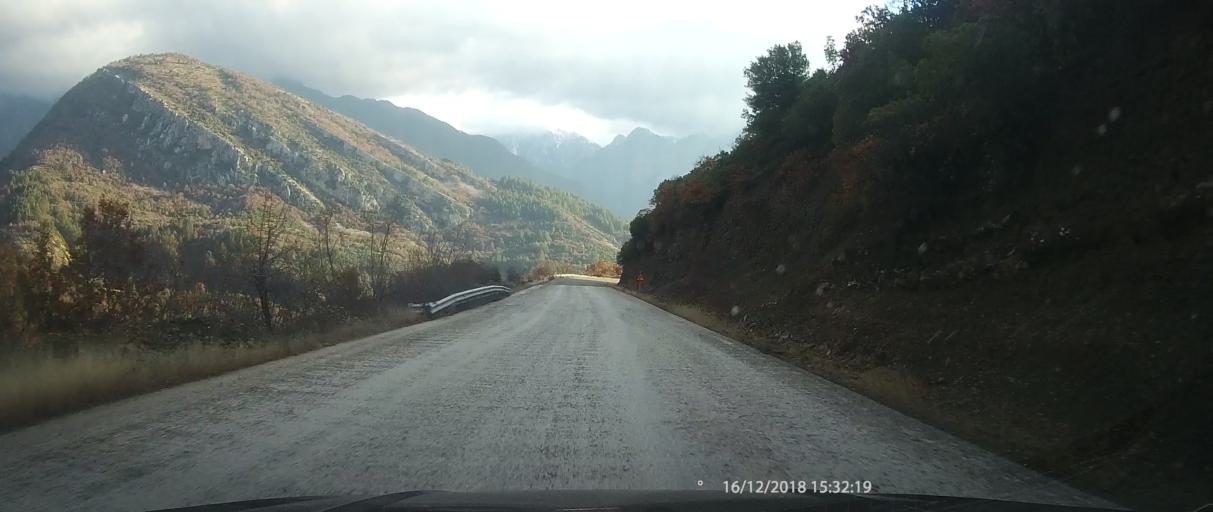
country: GR
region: Epirus
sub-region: Nomos Ioanninon
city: Konitsa
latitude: 40.0705
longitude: 20.7403
